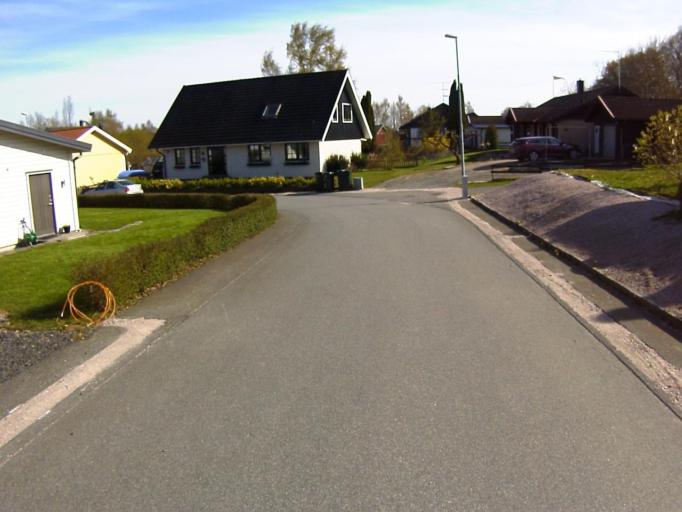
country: SE
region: Skane
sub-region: Kristianstads Kommun
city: Onnestad
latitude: 55.9973
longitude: 14.0354
